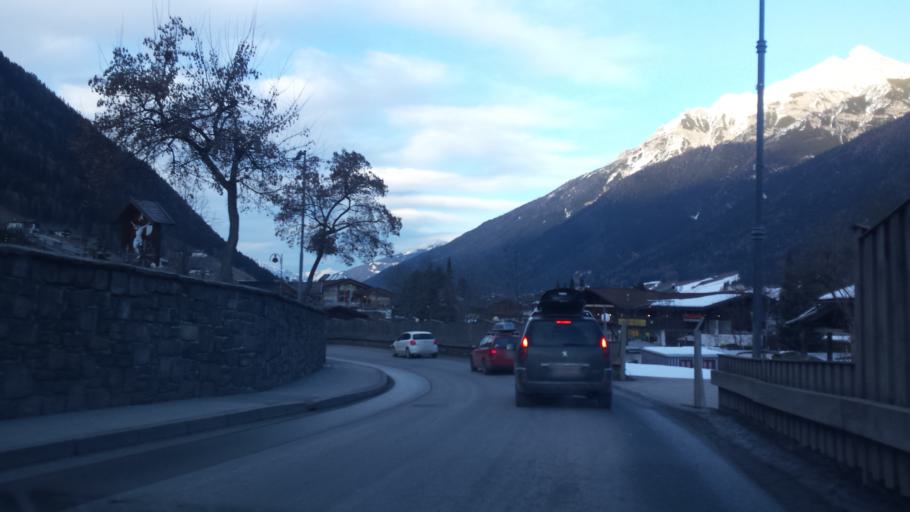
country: AT
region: Tyrol
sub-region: Politischer Bezirk Innsbruck Land
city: Neustift im Stubaital
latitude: 47.1097
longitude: 11.3073
